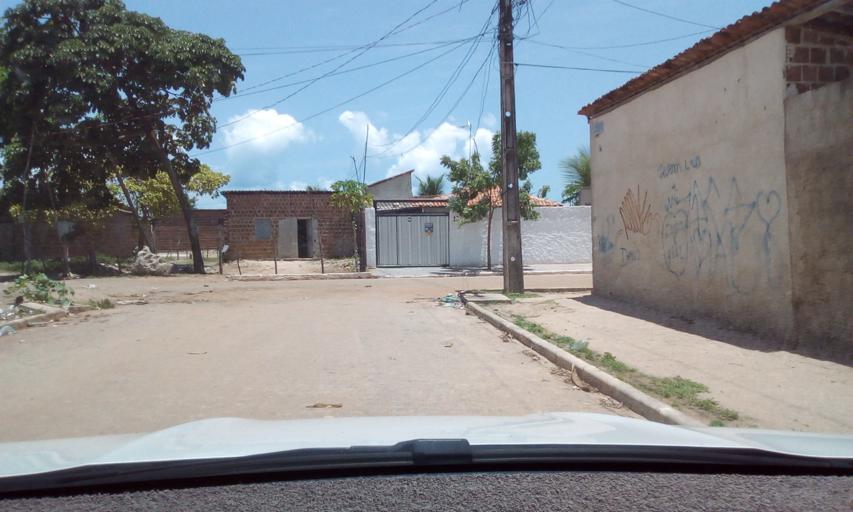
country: BR
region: Paraiba
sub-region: Joao Pessoa
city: Joao Pessoa
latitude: -7.1765
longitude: -34.8152
